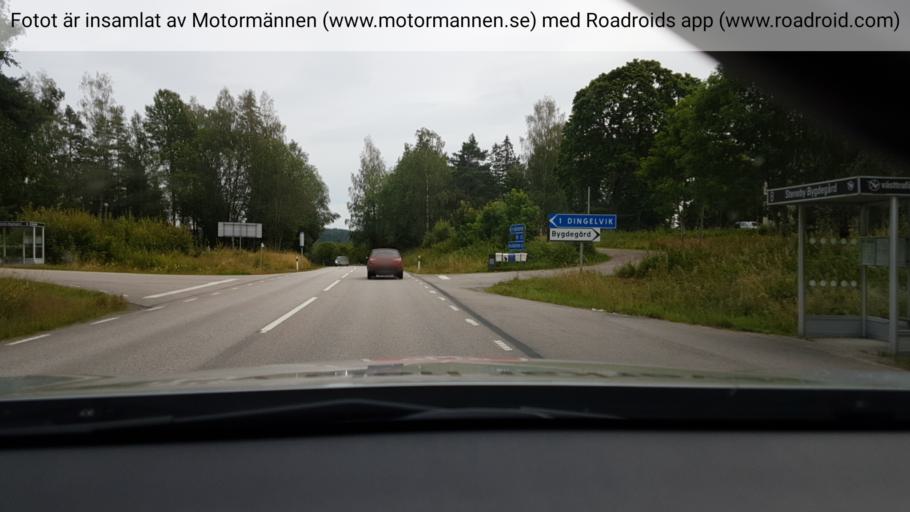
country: SE
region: Vaestra Goetaland
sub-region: Bengtsfors Kommun
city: Billingsfors
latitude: 58.9252
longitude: 12.2158
